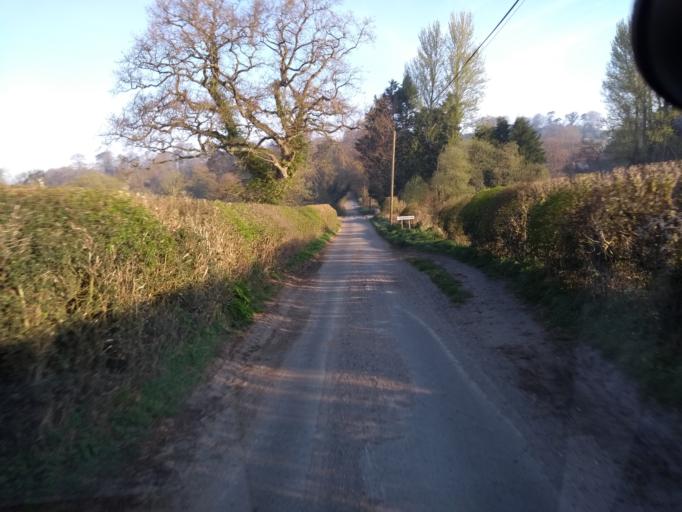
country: GB
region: England
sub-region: Somerset
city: Crewkerne
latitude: 50.8478
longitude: -2.8113
